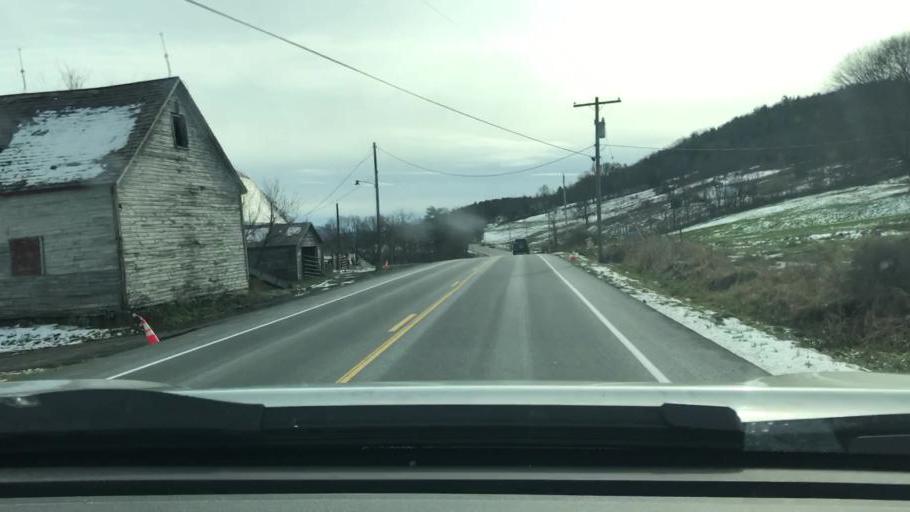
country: US
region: Vermont
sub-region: Rutland County
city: Poultney
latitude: 43.5514
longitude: -73.2579
